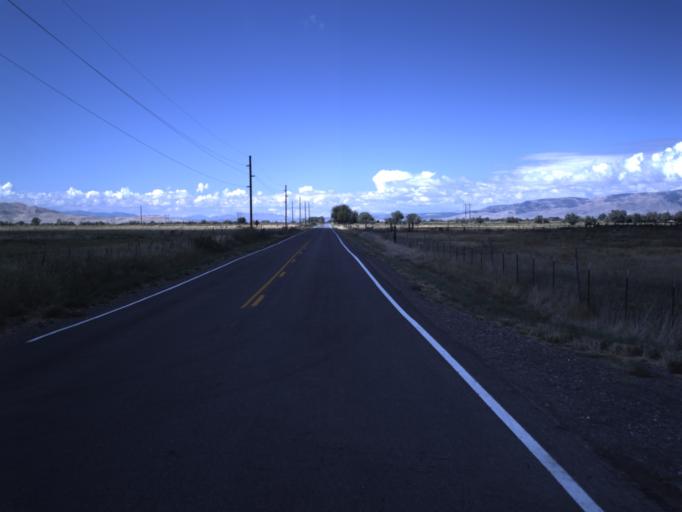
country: US
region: Utah
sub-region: Utah County
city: Spanish Fork
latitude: 40.1586
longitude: -111.6740
